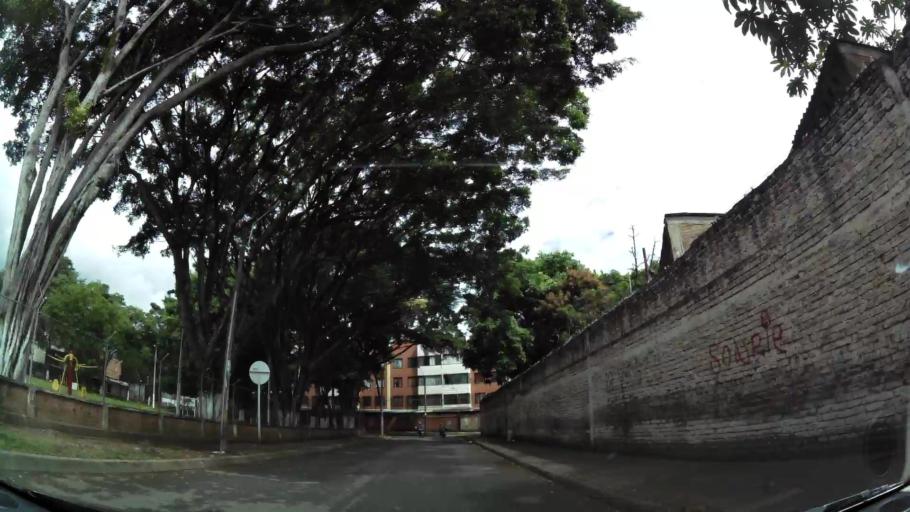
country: CO
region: Valle del Cauca
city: Cali
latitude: 3.3923
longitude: -76.5527
